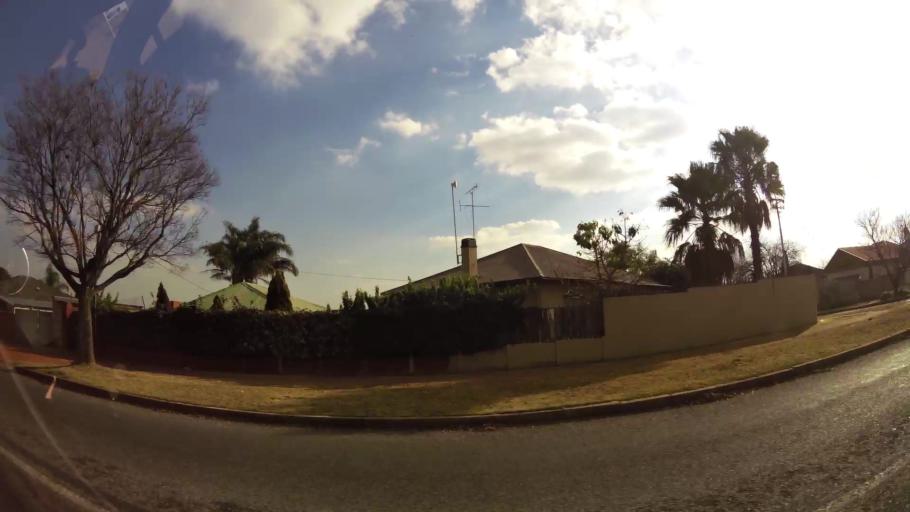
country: ZA
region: Gauteng
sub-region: West Rand District Municipality
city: Krugersdorp
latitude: -26.0860
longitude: 27.7677
